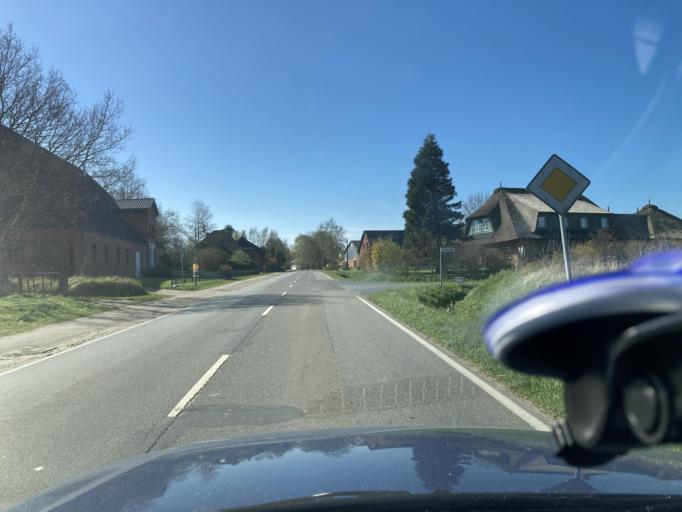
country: DE
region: Schleswig-Holstein
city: Odderade
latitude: 54.1416
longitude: 9.1910
